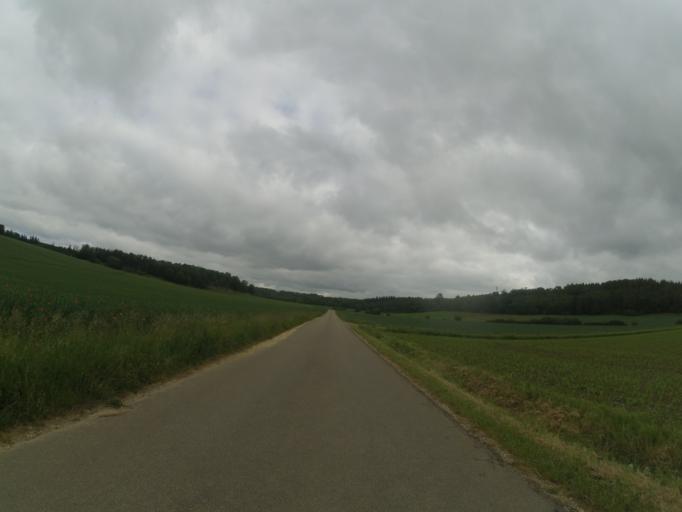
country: DE
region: Baden-Wuerttemberg
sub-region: Tuebingen Region
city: Bernstadt
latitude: 48.5089
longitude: 10.0296
